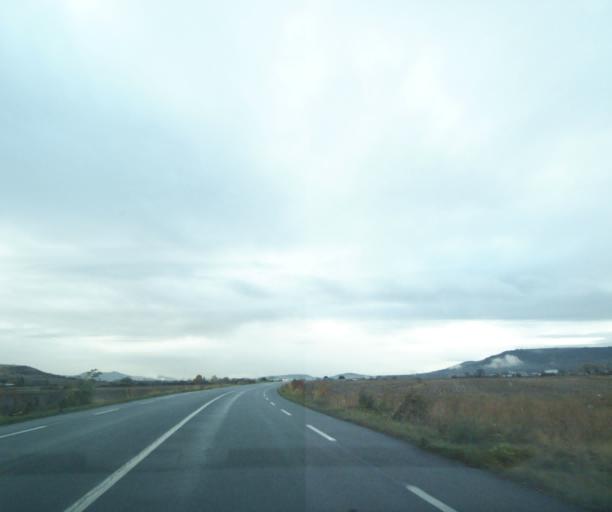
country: FR
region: Auvergne
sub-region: Departement du Puy-de-Dome
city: Perignat-les-Sarlieve
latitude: 45.7666
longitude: 3.1484
